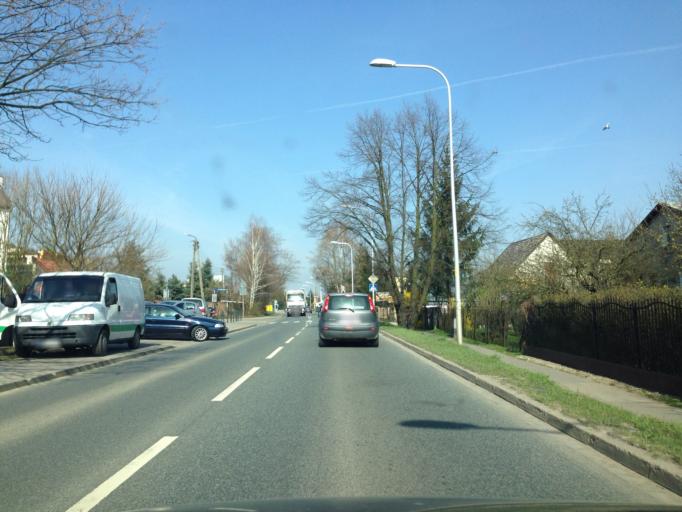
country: PL
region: Lower Silesian Voivodeship
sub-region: Powiat wroclawski
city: Wilczyce
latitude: 51.1078
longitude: 17.1416
